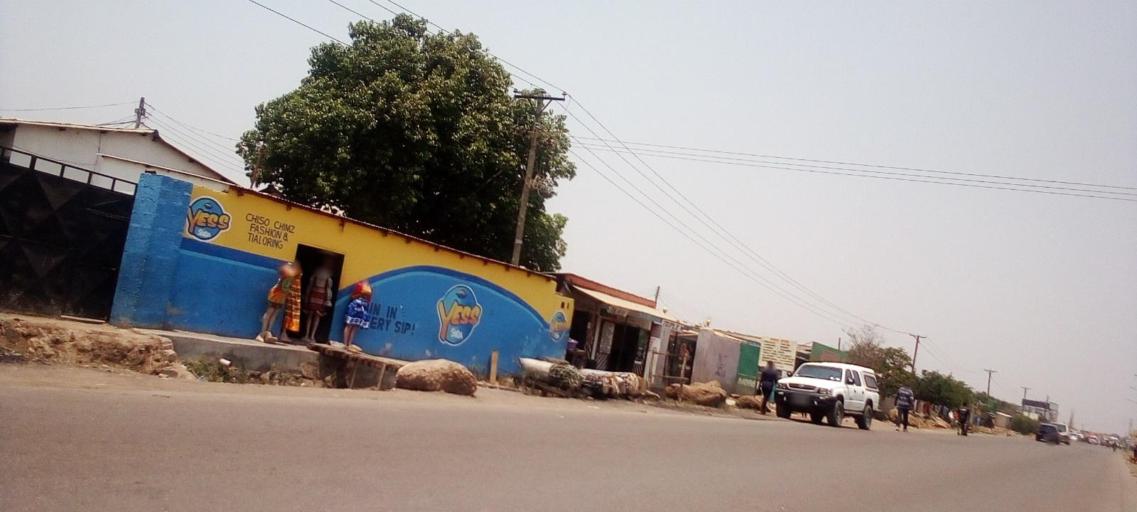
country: ZM
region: Lusaka
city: Lusaka
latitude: -15.4424
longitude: 28.2508
